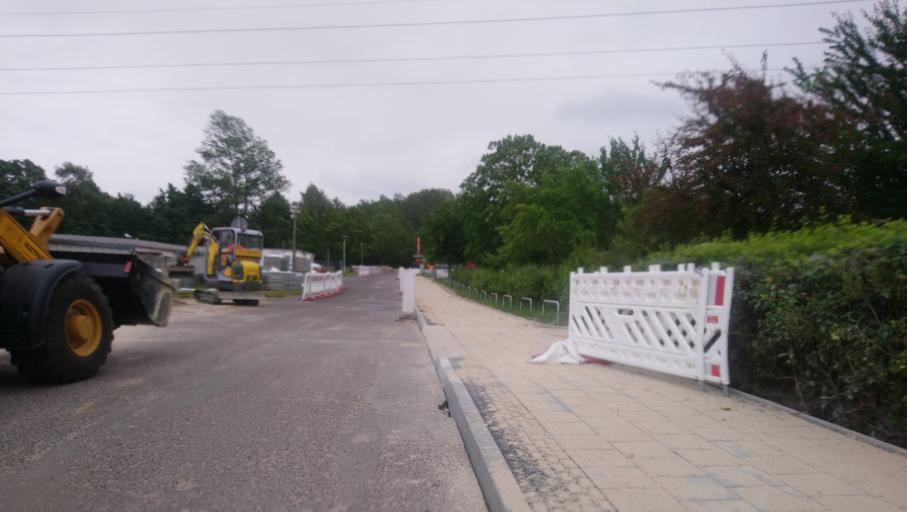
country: DE
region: Mecklenburg-Vorpommern
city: Rostock
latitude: 54.0686
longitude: 12.1086
